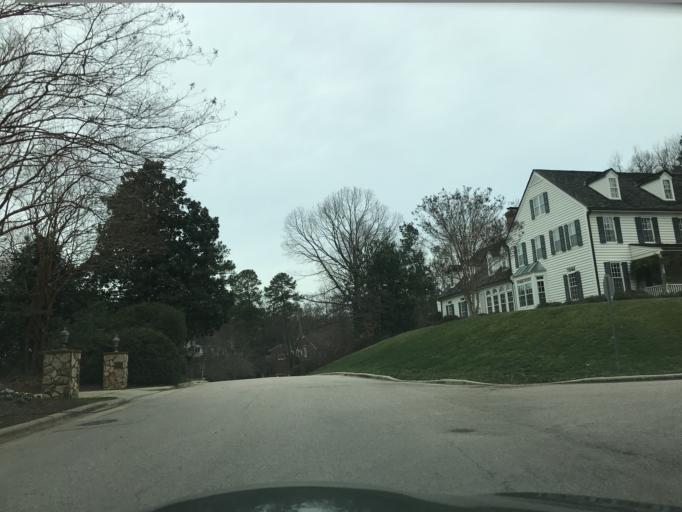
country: US
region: North Carolina
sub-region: Wake County
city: West Raleigh
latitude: 35.8819
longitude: -78.6073
